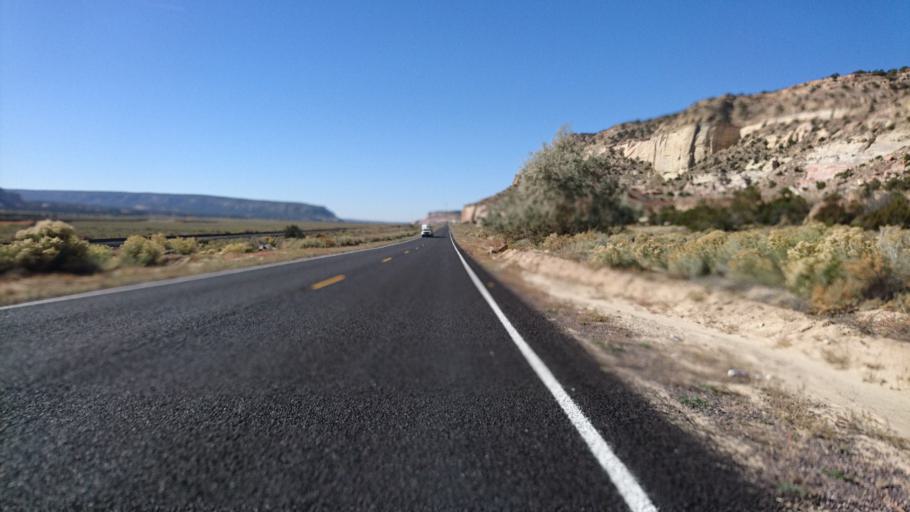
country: US
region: Arizona
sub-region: Apache County
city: Houck
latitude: 35.4092
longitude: -109.0056
